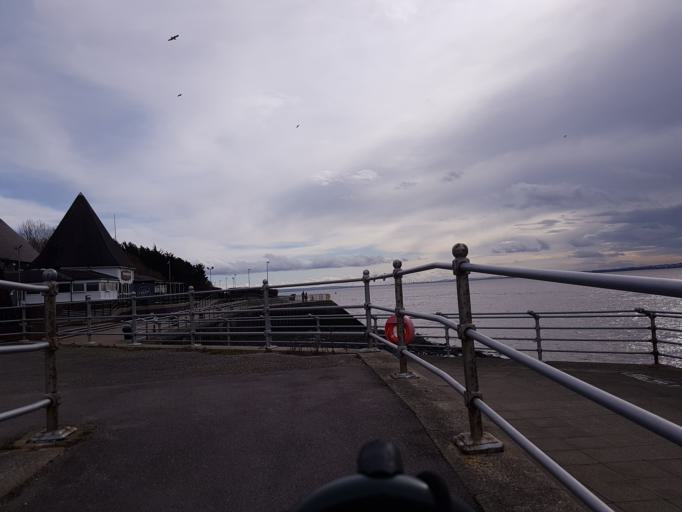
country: GB
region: England
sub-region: Metropolitan Borough of Wirral
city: Bromborough
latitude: 53.3741
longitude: -2.9648
